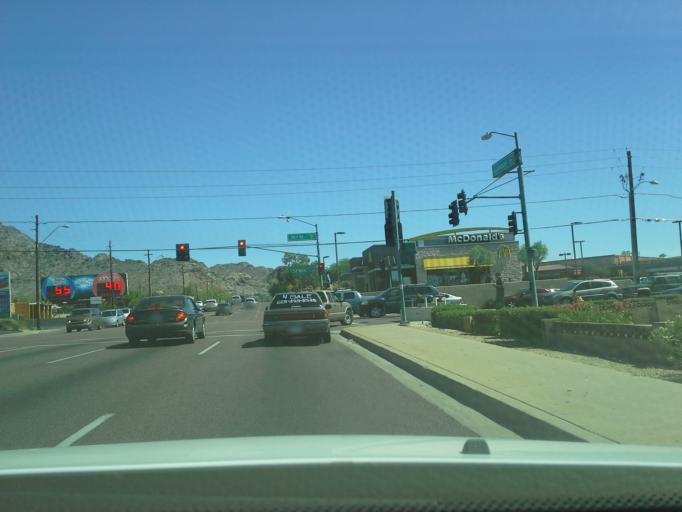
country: US
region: Arizona
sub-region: Maricopa County
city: Phoenix
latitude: 33.5382
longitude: -112.0479
